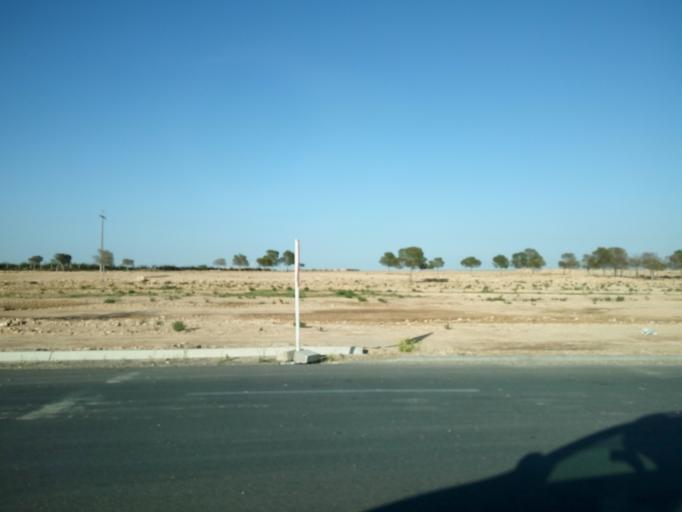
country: DZ
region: Djelfa
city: Ain Oussera
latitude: 35.3011
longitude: 2.9725
